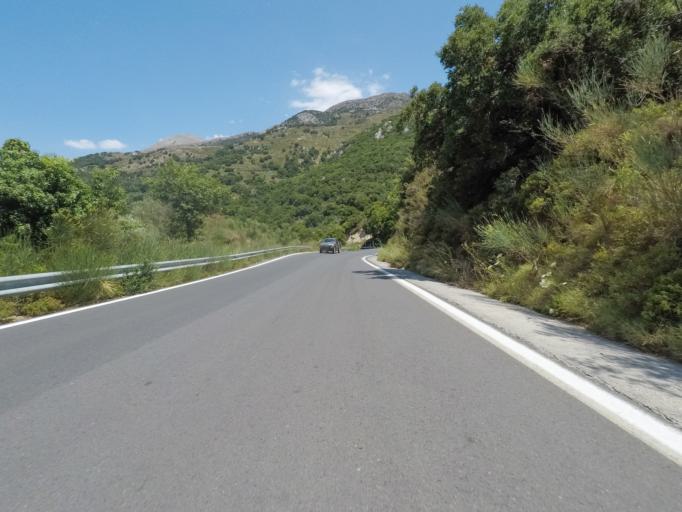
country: GR
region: Crete
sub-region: Nomos Irakleiou
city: Mokhos
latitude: 35.2304
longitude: 25.4598
